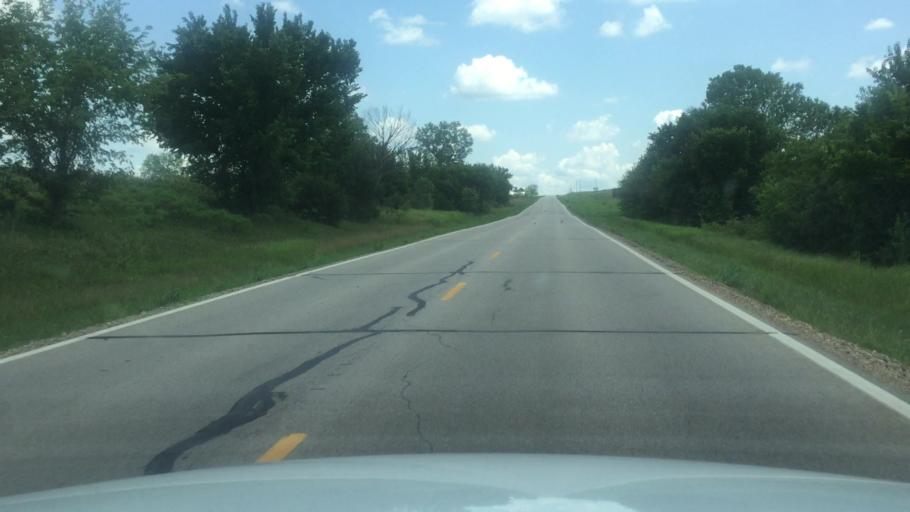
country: US
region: Kansas
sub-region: Brown County
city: Horton
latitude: 39.6674
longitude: -95.6263
